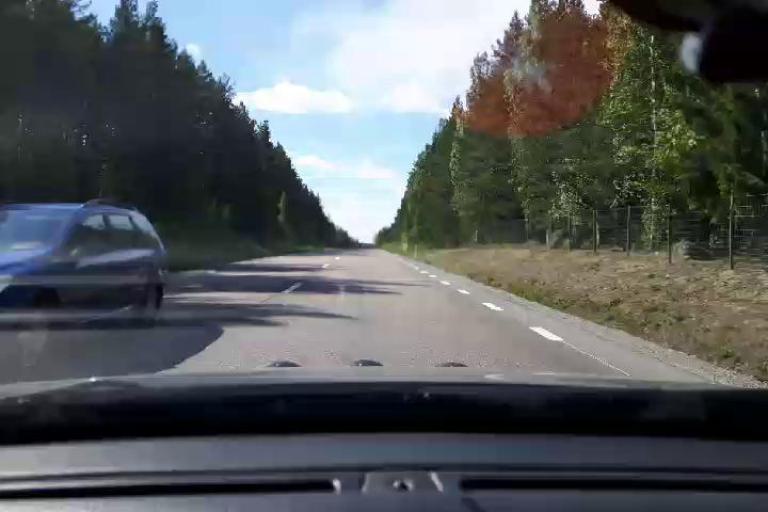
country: SE
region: Gaevleborg
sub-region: Bollnas Kommun
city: Bollnas
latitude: 61.2981
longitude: 16.4837
